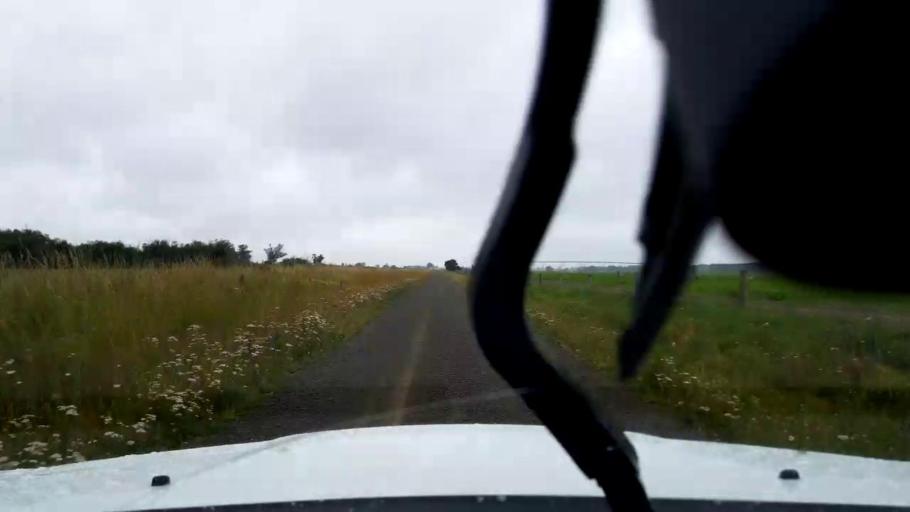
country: NZ
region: Canterbury
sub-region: Timaru District
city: Pleasant Point
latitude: -44.2540
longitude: 171.1898
